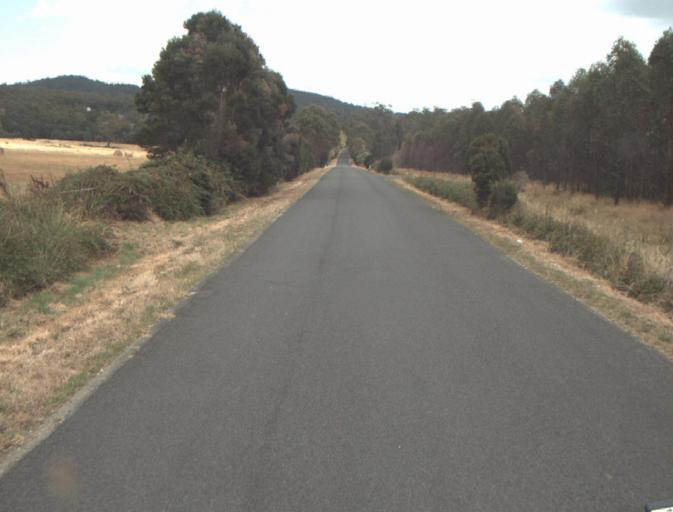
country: AU
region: Tasmania
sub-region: Launceston
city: Mayfield
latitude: -41.2113
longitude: 147.0568
